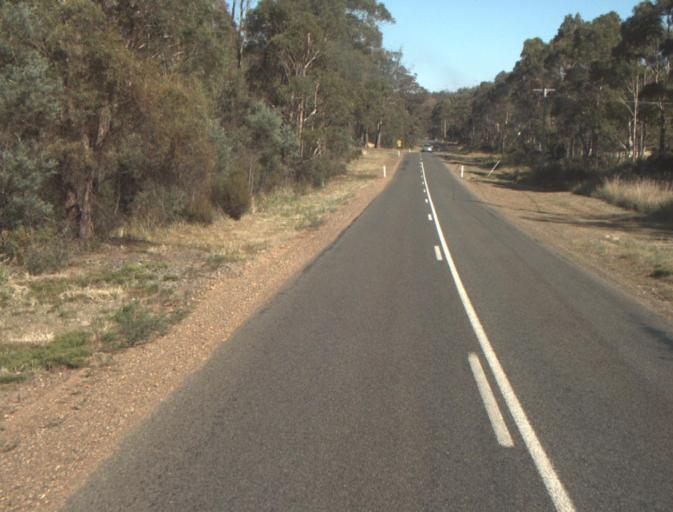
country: AU
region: Tasmania
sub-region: Launceston
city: Mayfield
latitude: -41.3155
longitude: 147.1352
